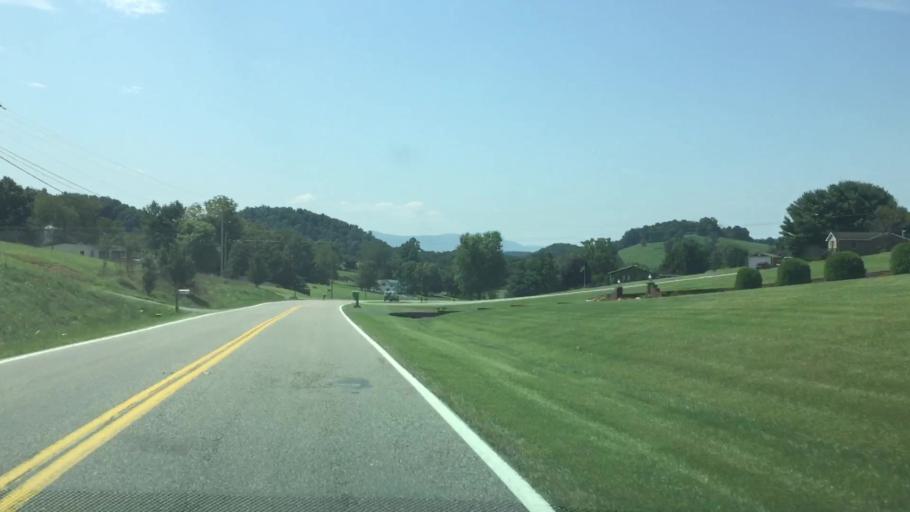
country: US
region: Virginia
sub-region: Washington County
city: Abingdon
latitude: 36.6624
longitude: -81.9666
